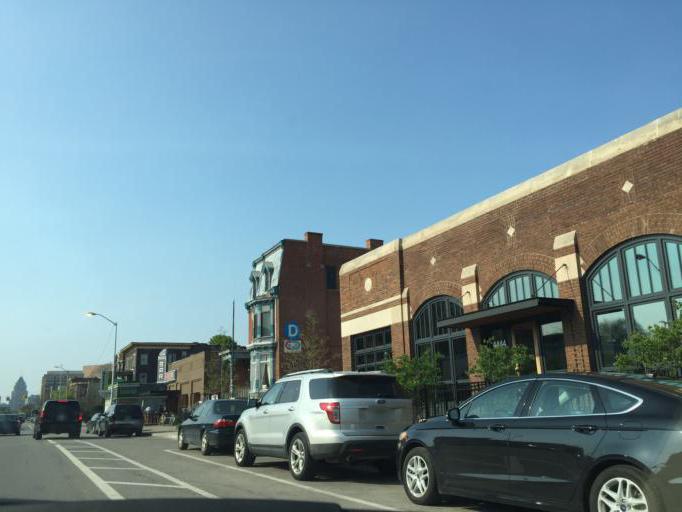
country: US
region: Michigan
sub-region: Wayne County
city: Detroit
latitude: 42.3518
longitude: -83.0668
